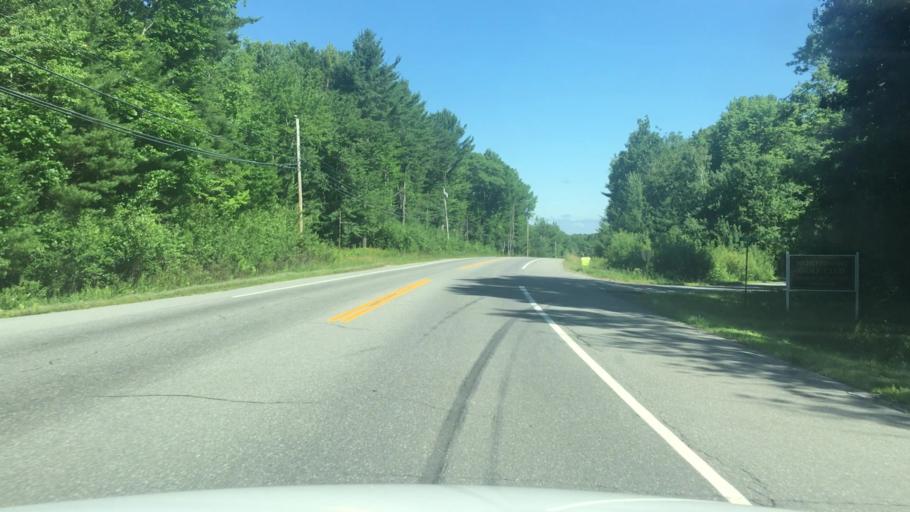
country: US
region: Maine
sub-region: Waldo County
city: Northport
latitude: 44.3726
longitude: -68.9838
